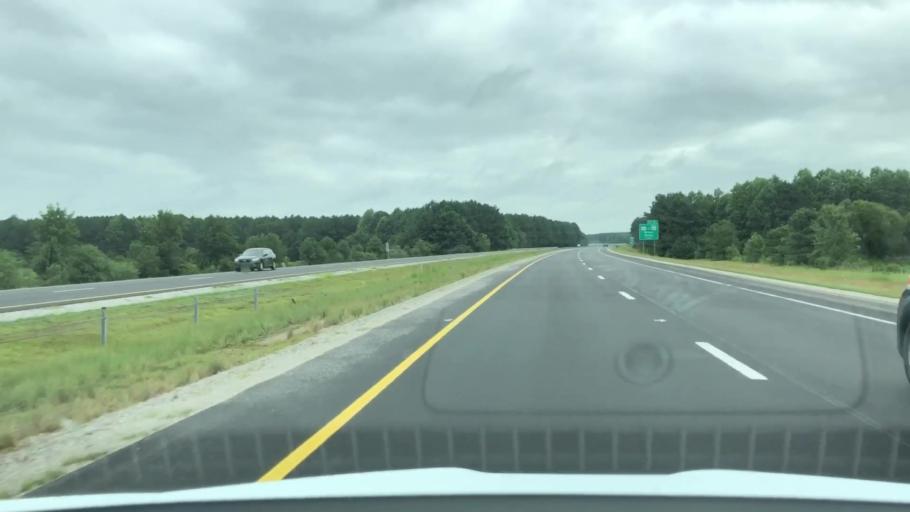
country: US
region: North Carolina
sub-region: Wilson County
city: Lucama
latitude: 35.6491
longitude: -77.9619
